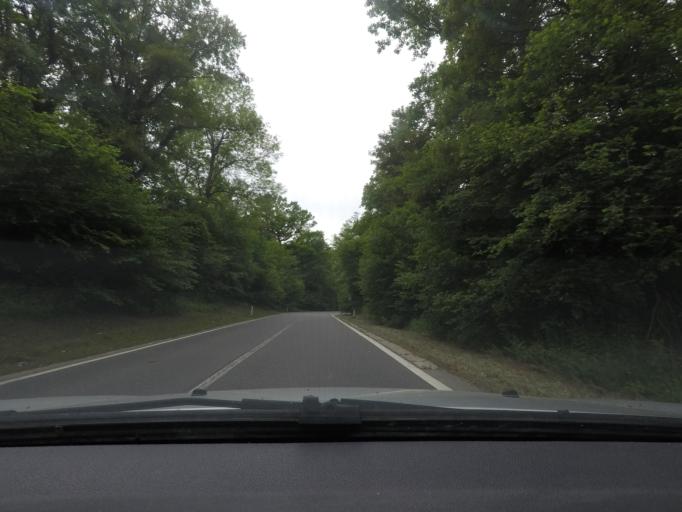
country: BE
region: Wallonia
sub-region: Province de Namur
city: Noville-les-Bois
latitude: 50.5148
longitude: 4.9908
